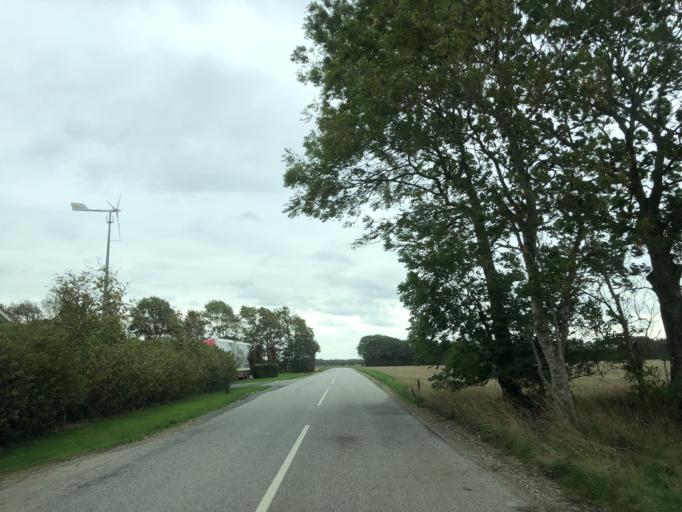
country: DK
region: Central Jutland
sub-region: Herning Kommune
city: Snejbjerg
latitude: 56.1473
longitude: 8.8963
